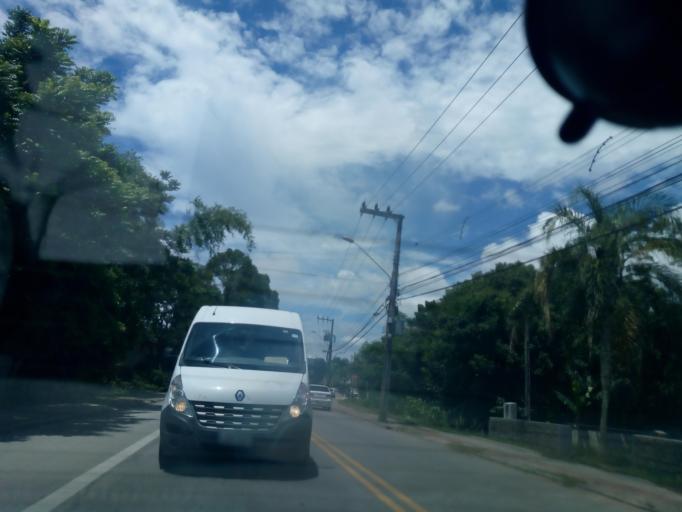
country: BR
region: Santa Catarina
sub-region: Florianopolis
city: Itacorubi
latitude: -27.4090
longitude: -48.4242
